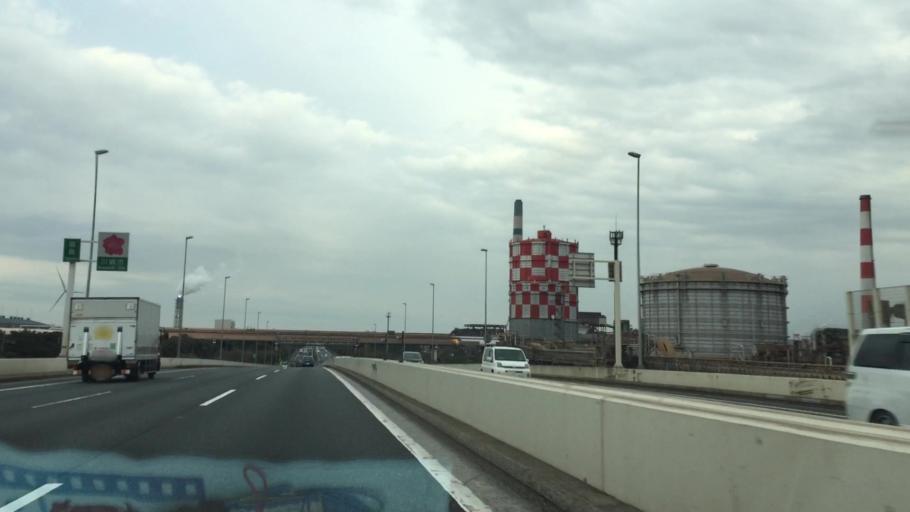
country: JP
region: Kanagawa
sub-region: Kawasaki-shi
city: Kawasaki
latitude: 35.4822
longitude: 139.7182
